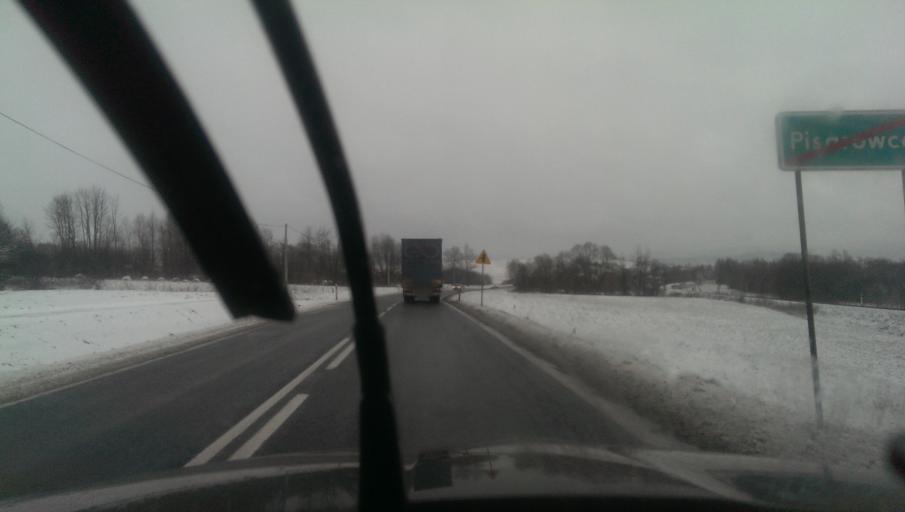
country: PL
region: Subcarpathian Voivodeship
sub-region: Powiat sanocki
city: Nowosielce-Gniewosz
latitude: 49.5623
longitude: 22.1163
